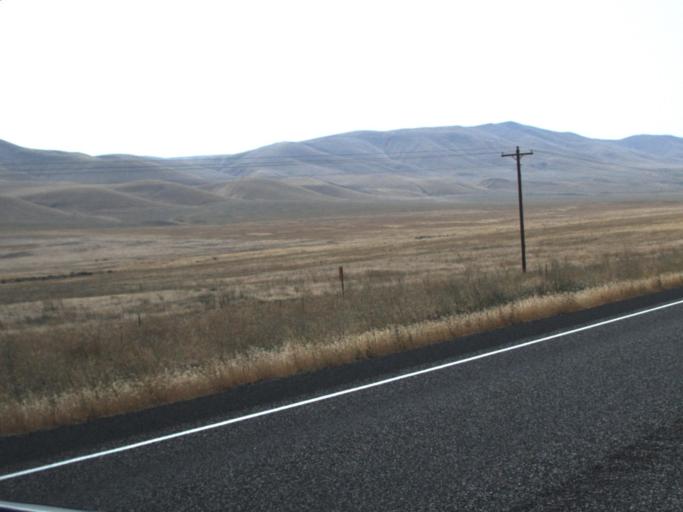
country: US
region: Washington
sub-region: Grant County
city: Desert Aire
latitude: 46.5297
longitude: -119.9341
